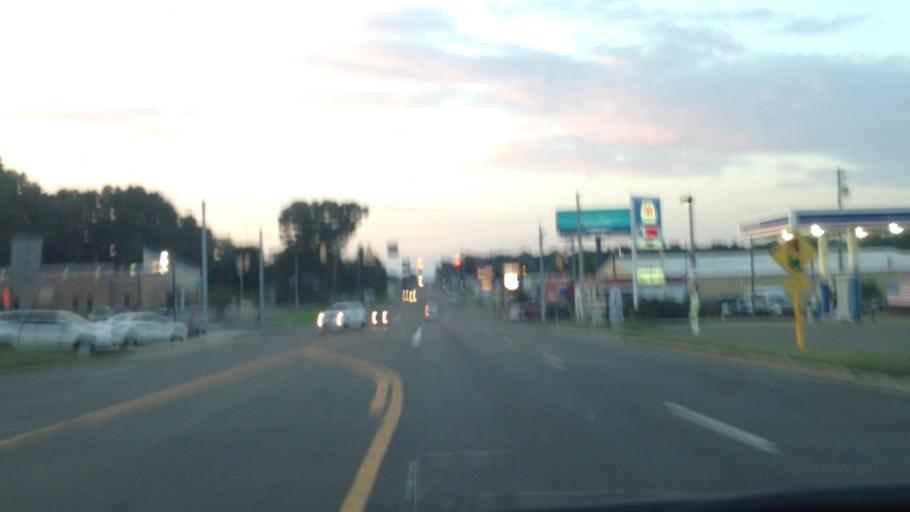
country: US
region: Ohio
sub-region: Stark County
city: Canton
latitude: 40.8101
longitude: -81.4255
